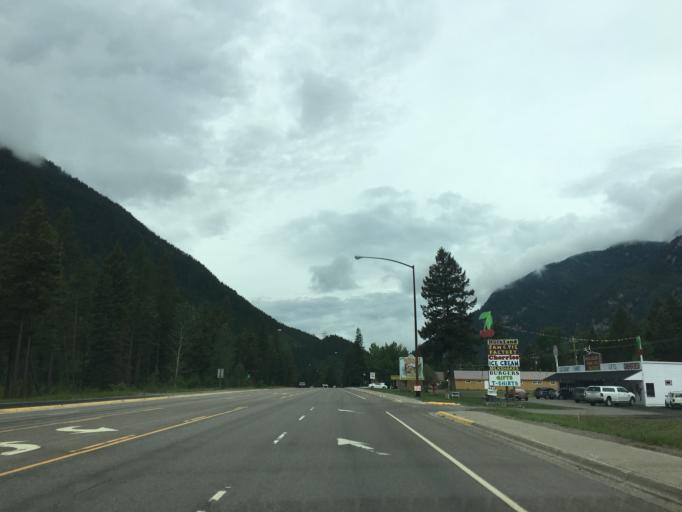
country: US
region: Montana
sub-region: Flathead County
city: Columbia Falls
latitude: 48.3857
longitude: -114.0692
